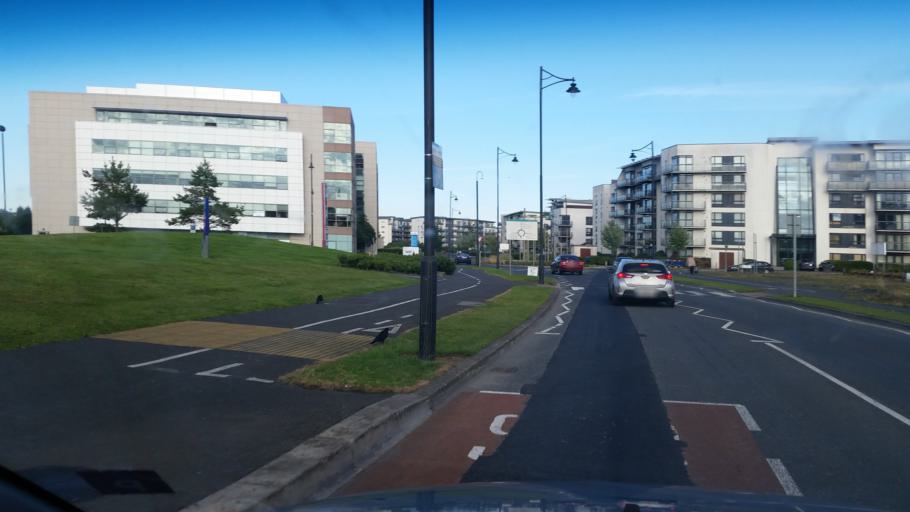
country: IE
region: Leinster
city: Ballymun
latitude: 53.4031
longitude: -6.2596
